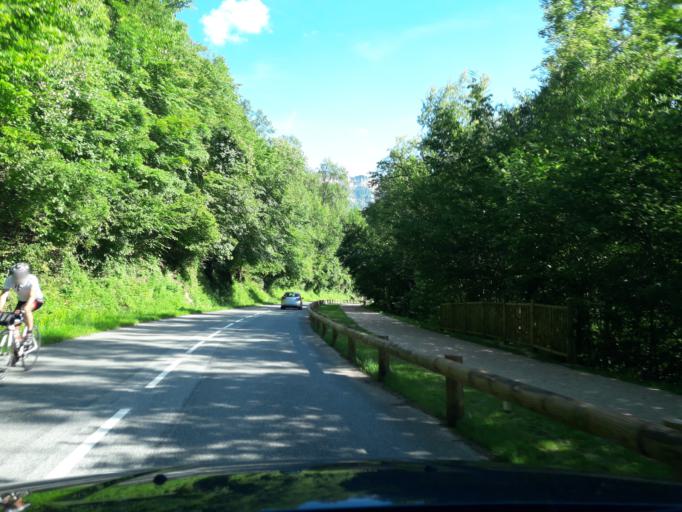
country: FR
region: Rhone-Alpes
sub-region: Departement de la Savoie
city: Vimines
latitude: 45.5616
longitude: 5.8123
